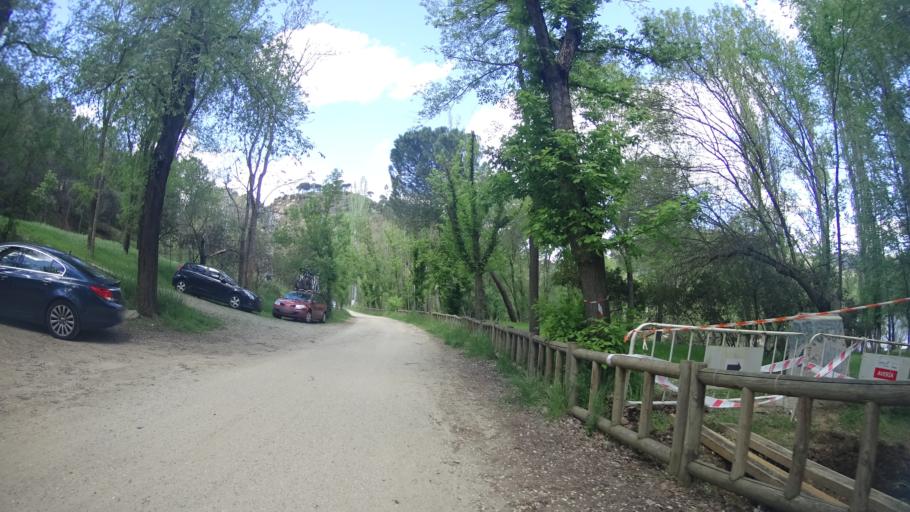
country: ES
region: Madrid
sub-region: Provincia de Madrid
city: Pelayos de la Presa
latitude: 40.3660
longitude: -4.3049
